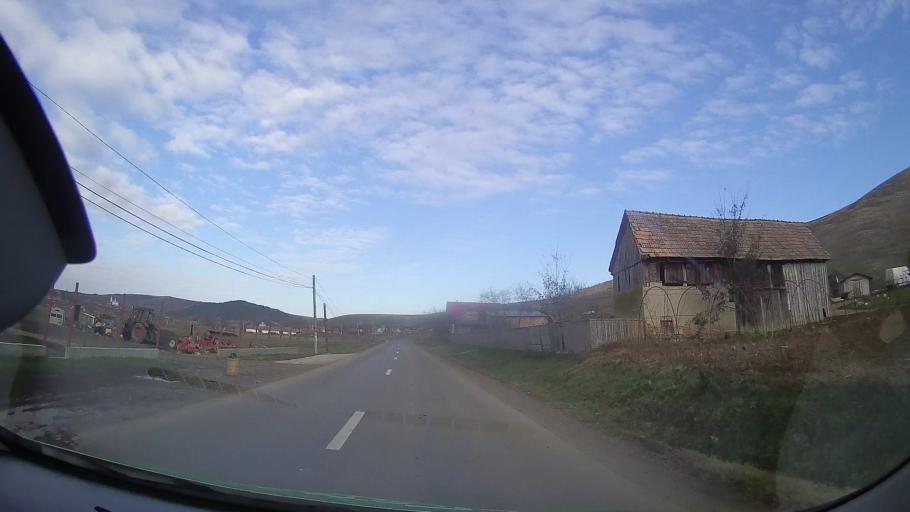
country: RO
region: Mures
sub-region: Comuna Iclanzel
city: Iclanzel
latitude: 46.5149
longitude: 24.2739
